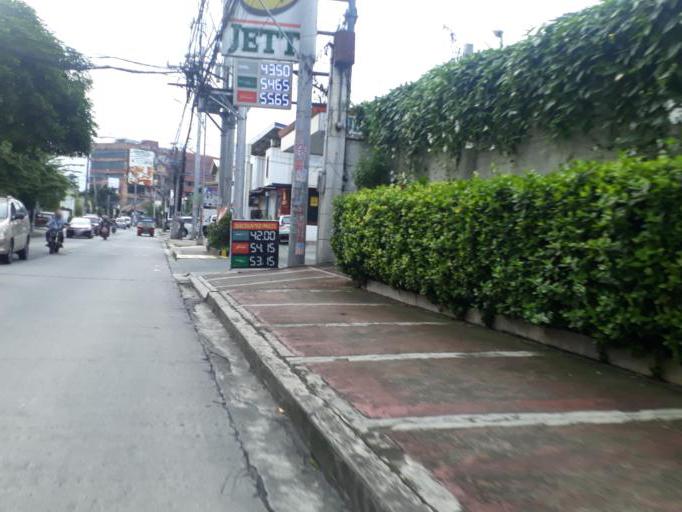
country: PH
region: Metro Manila
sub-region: Quezon City
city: Quezon City
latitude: 14.6358
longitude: 121.0673
